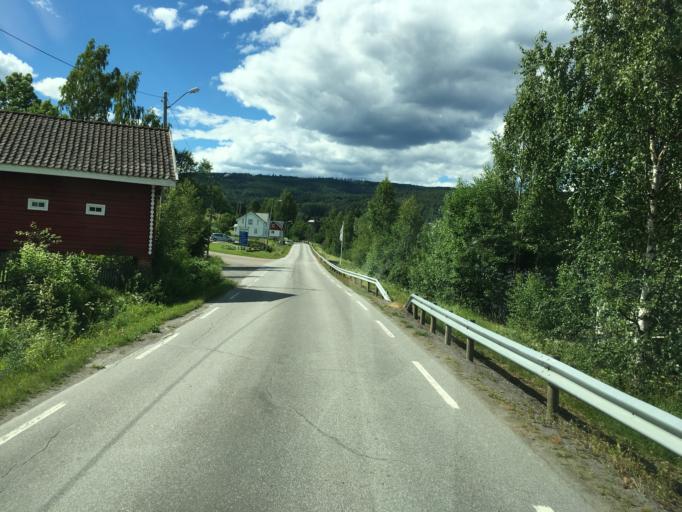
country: NO
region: Oppland
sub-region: Sondre Land
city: Hov
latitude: 60.5179
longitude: 10.2961
